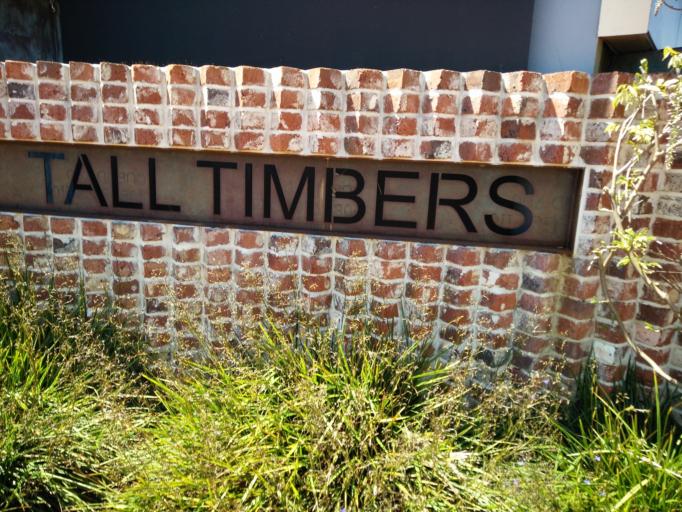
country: AU
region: Western Australia
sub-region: Manjimup
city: Manjimup
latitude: -34.2404
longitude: 116.1472
